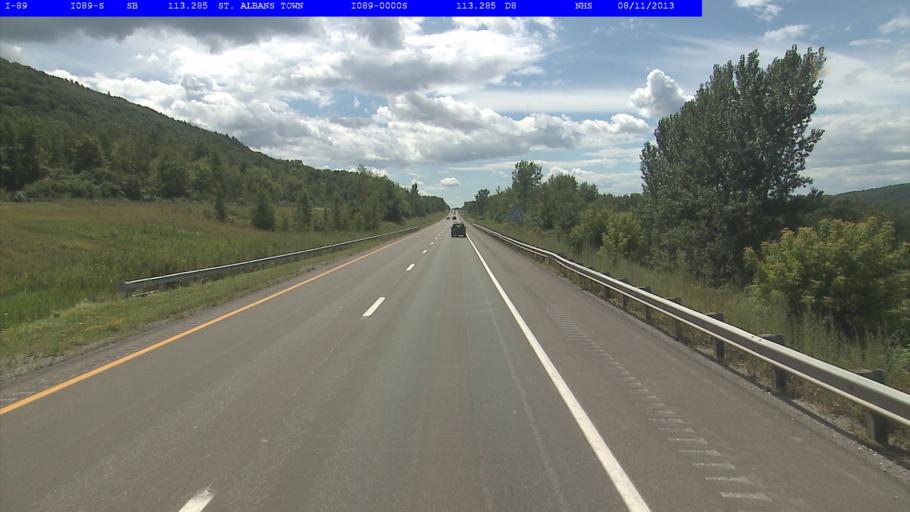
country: US
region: Vermont
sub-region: Franklin County
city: Saint Albans
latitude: 44.7884
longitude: -73.0723
